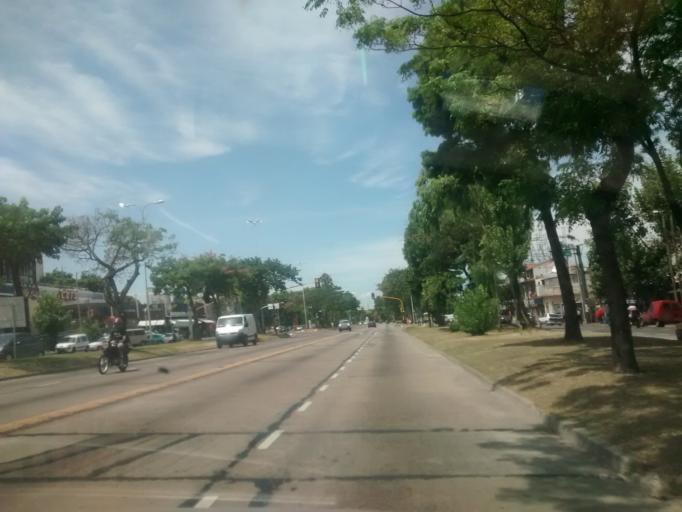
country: AR
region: Buenos Aires
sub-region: Partido de Avellaneda
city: Avellaneda
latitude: -34.6837
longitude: -58.3430
